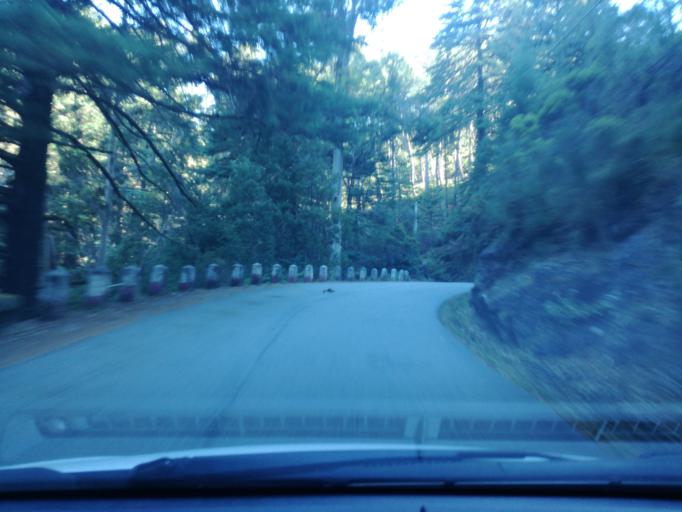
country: PT
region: Braga
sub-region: Vieira do Minho
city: Real
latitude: 41.7435
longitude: -8.1542
